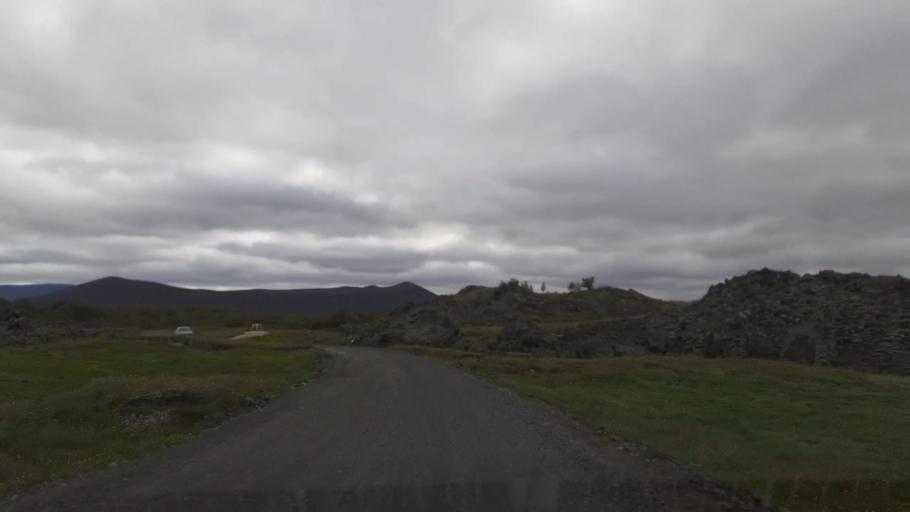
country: IS
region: Northeast
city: Laugar
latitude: 65.6227
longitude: -16.9128
